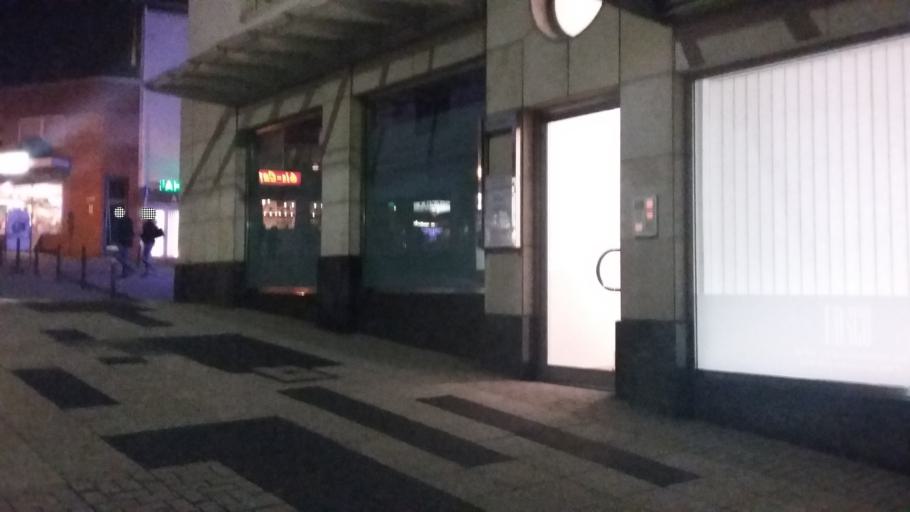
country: DE
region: North Rhine-Westphalia
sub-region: Regierungsbezirk Dusseldorf
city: Wuppertal
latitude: 51.2600
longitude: 7.1446
